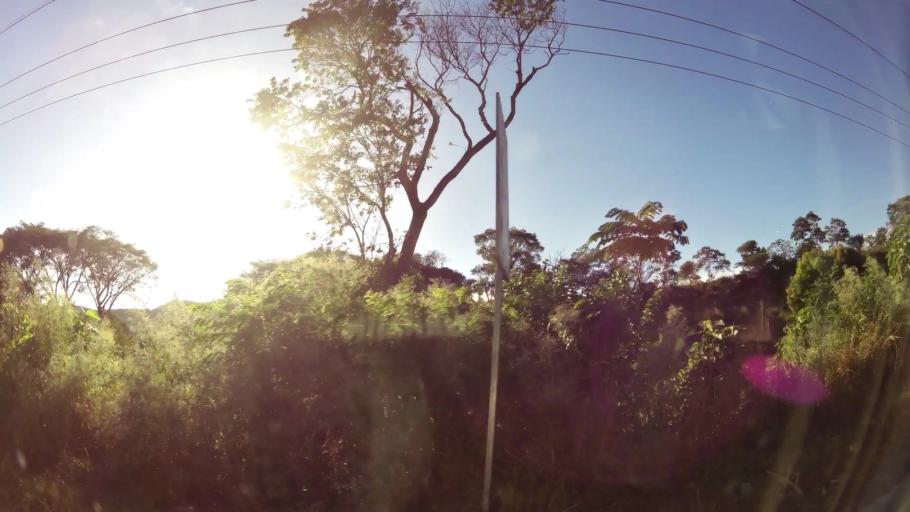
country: SV
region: Santa Ana
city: Metapan
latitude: 14.2846
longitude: -89.4618
